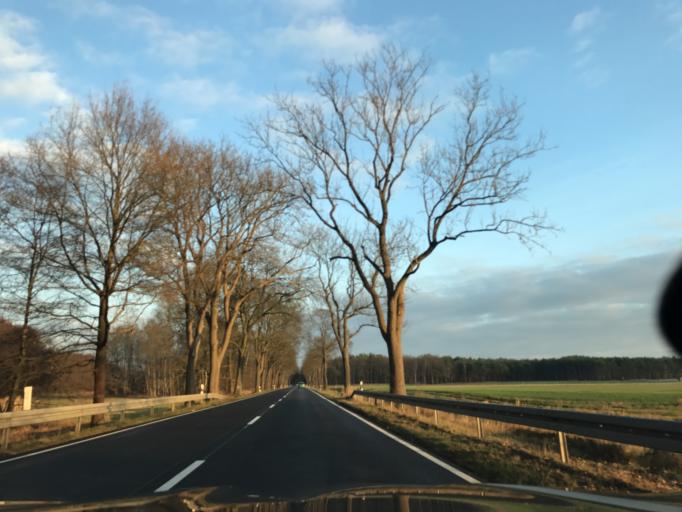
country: DE
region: Brandenburg
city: Bensdorf
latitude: 52.4111
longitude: 12.3033
